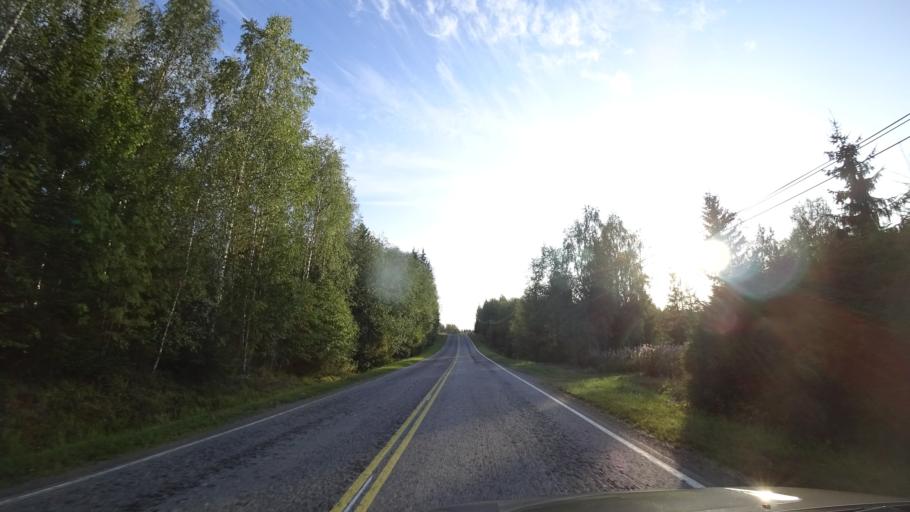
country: FI
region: Haeme
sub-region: Haemeenlinna
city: Lammi
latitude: 61.0376
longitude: 24.9316
